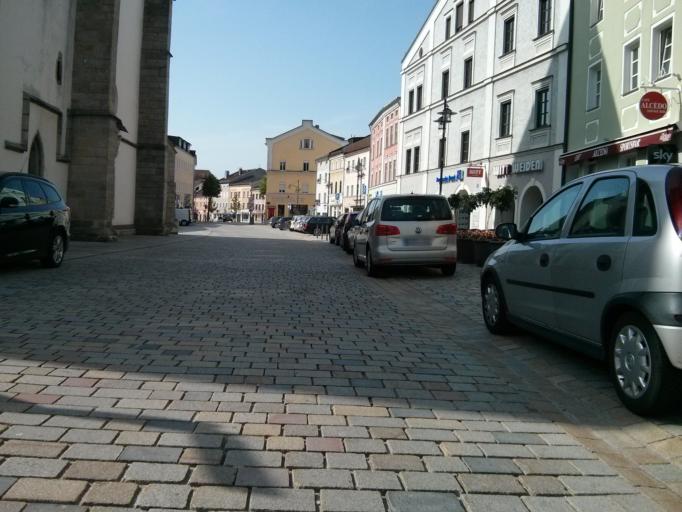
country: DE
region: Bavaria
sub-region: Lower Bavaria
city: Deggendorf
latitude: 48.8320
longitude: 12.9620
